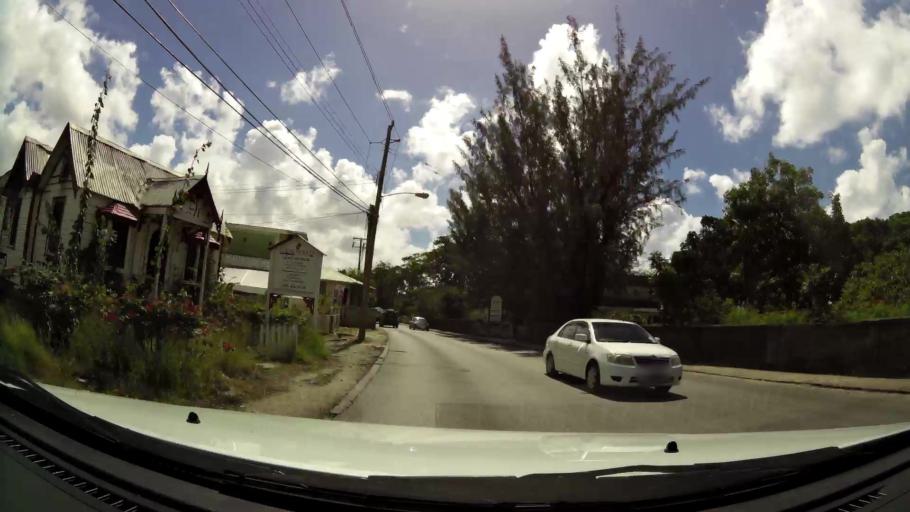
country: BB
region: Saint James
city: Holetown
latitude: 13.1916
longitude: -59.6385
